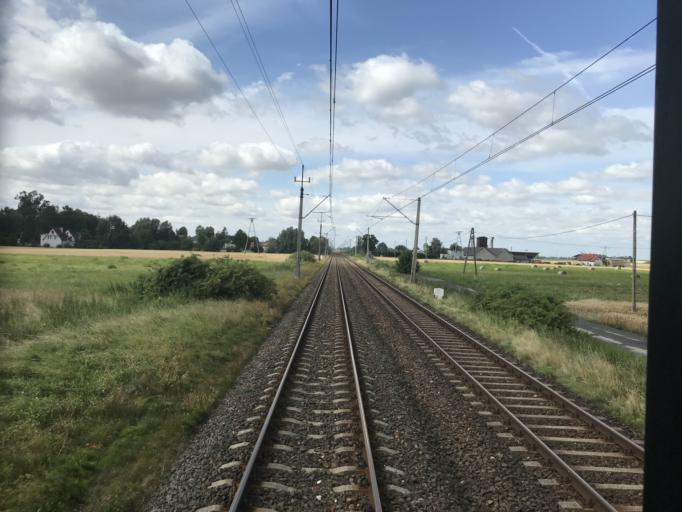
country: PL
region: Warmian-Masurian Voivodeship
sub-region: Powiat elblaski
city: Gronowo Elblaskie
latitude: 54.0832
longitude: 19.2890
